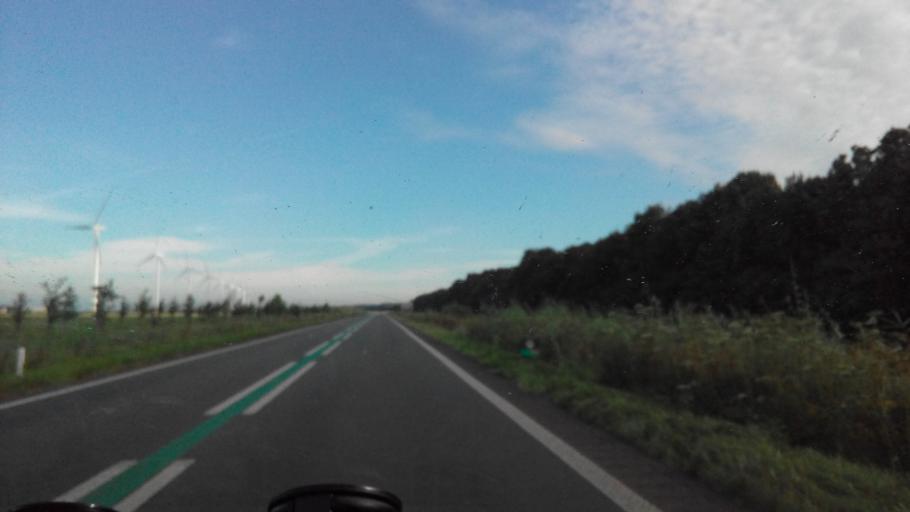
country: NL
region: Gelderland
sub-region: Gemeente Nijkerk
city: Nijkerk
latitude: 52.2865
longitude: 5.4596
